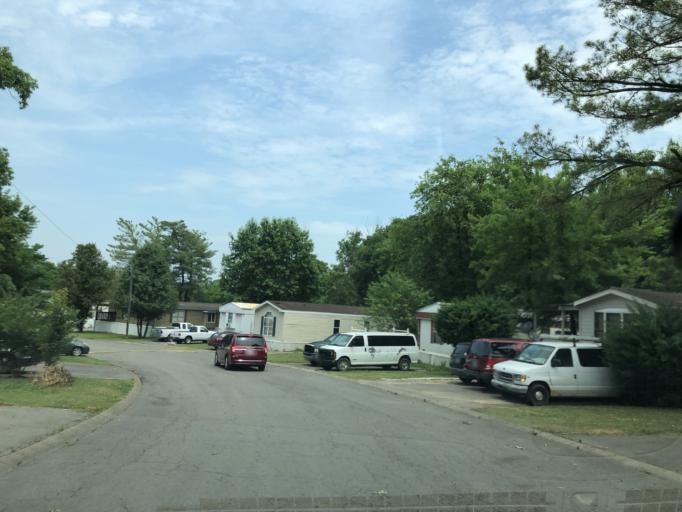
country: US
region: Tennessee
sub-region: Davidson County
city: Oak Hill
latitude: 36.0748
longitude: -86.6765
